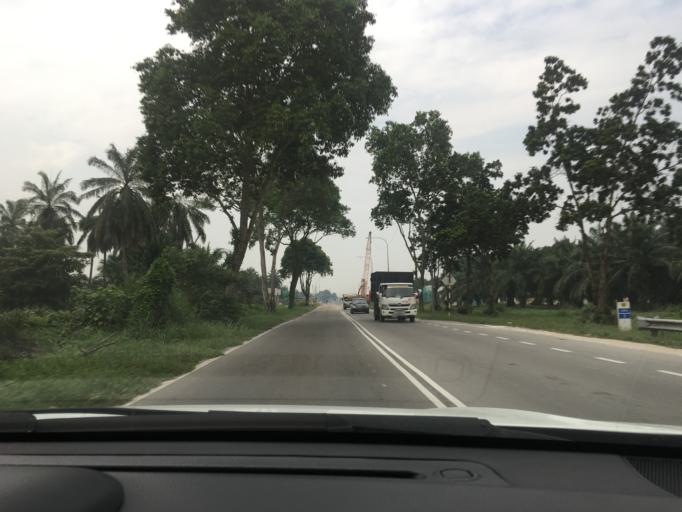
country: MY
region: Selangor
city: Klang
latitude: 3.1362
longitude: 101.4024
